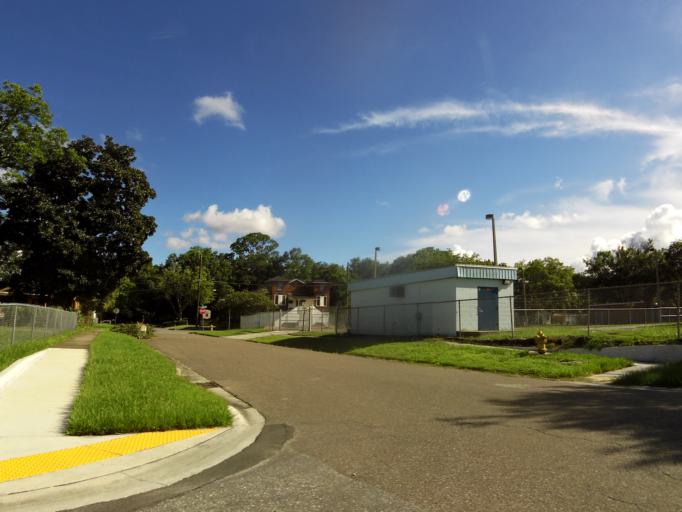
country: US
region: Florida
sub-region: Duval County
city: Jacksonville
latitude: 30.3377
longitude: -81.6957
